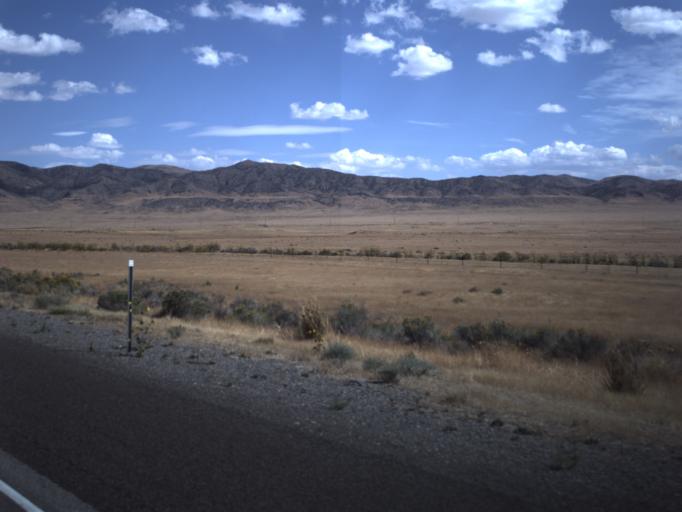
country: US
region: Utah
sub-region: Tooele County
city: Grantsville
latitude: 40.7627
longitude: -113.0003
